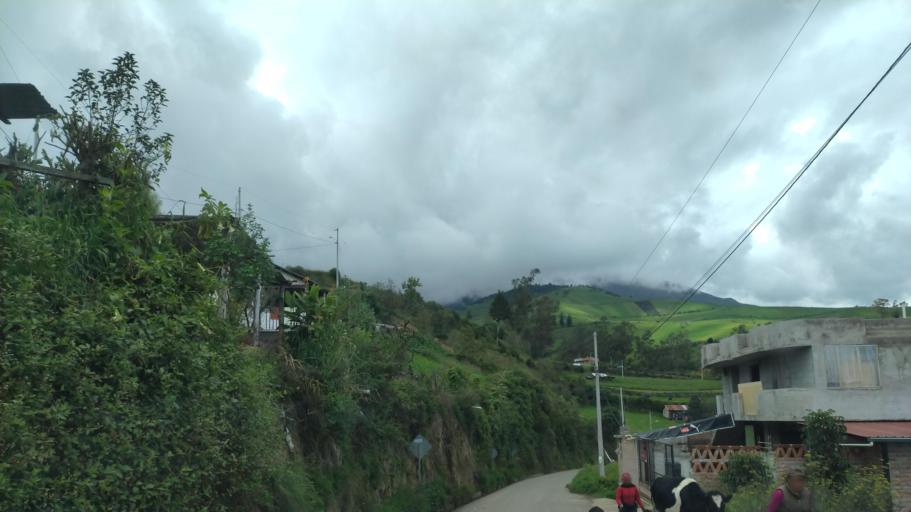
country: EC
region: Chimborazo
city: Riobamba
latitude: -1.6803
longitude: -78.5747
